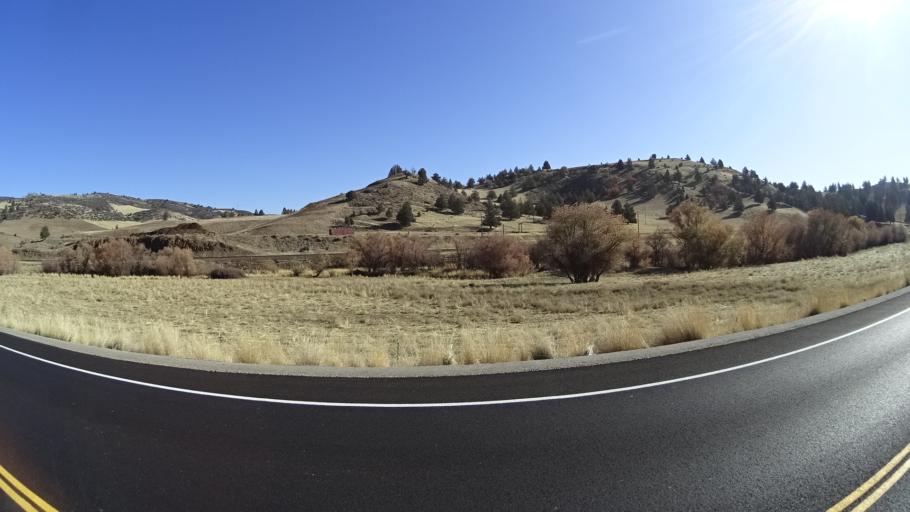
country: US
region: California
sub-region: Siskiyou County
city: Montague
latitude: 41.8633
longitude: -122.4649
